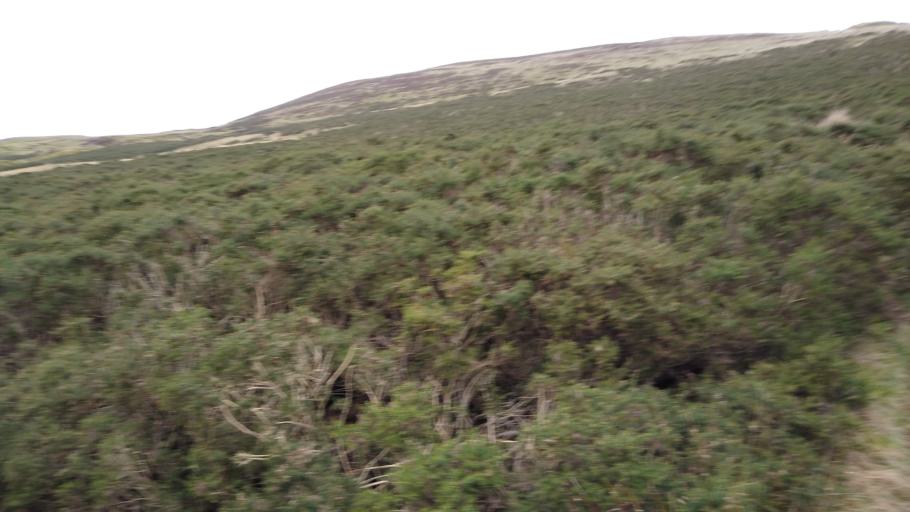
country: GB
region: England
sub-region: Cumbria
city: Frizington
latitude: 54.5538
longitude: -3.4042
